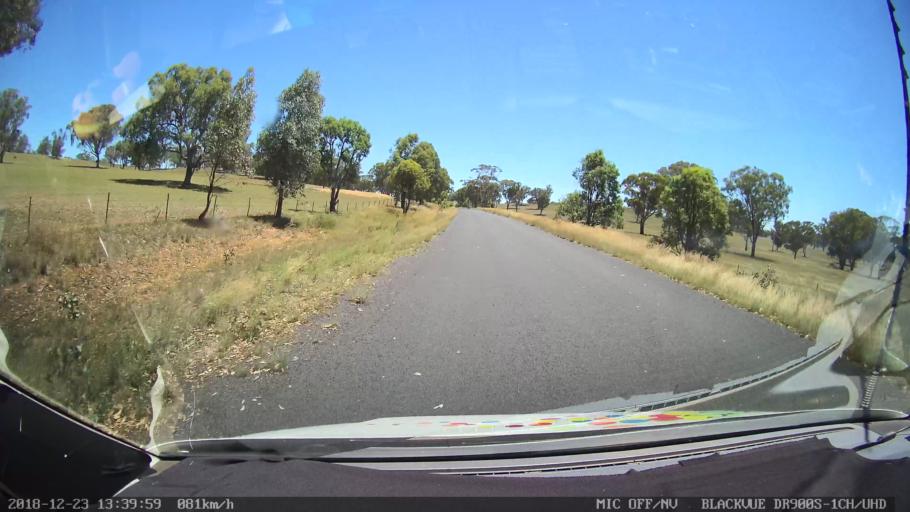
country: AU
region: New South Wales
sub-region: Armidale Dumaresq
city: Armidale
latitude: -30.4629
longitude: 151.1959
